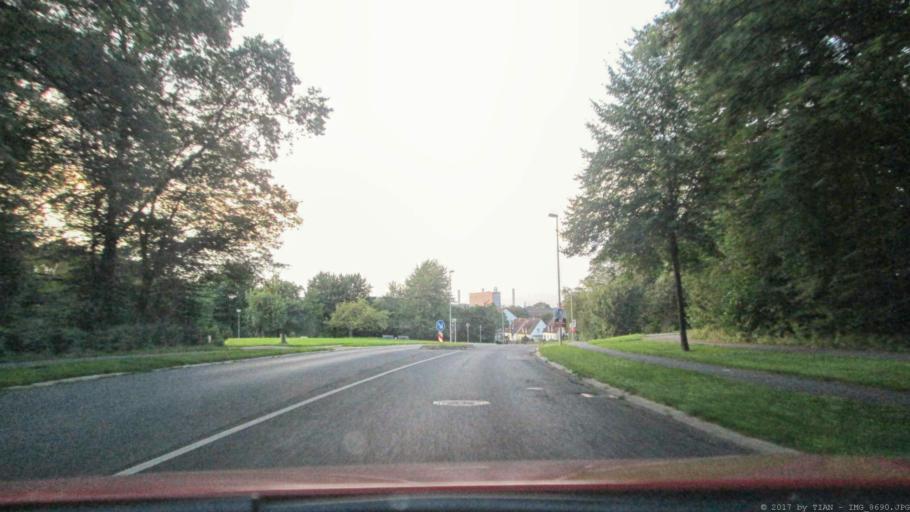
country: DE
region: Lower Saxony
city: Wolfsburg
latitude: 52.4171
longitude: 10.7606
